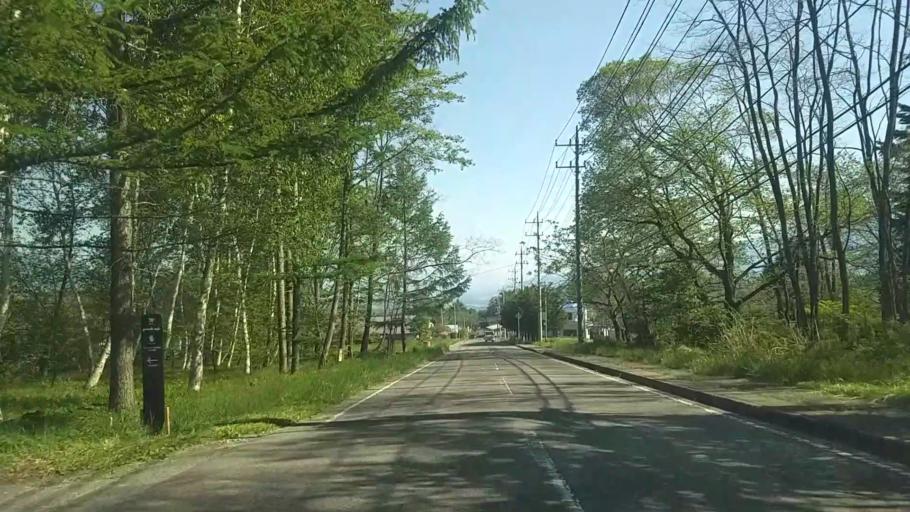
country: JP
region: Yamanashi
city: Nirasaki
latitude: 35.9008
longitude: 138.4097
